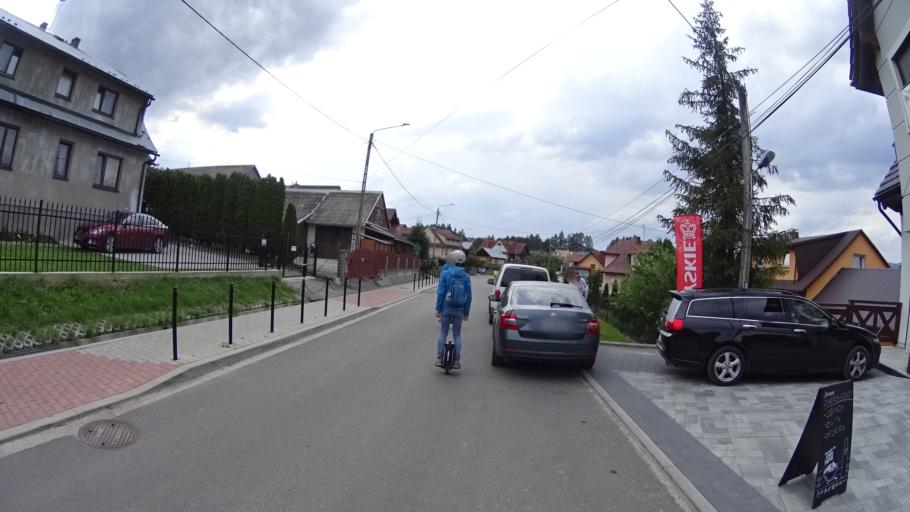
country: PL
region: Lesser Poland Voivodeship
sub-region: Powiat nowotarski
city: Niedzica
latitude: 49.4233
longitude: 20.3128
